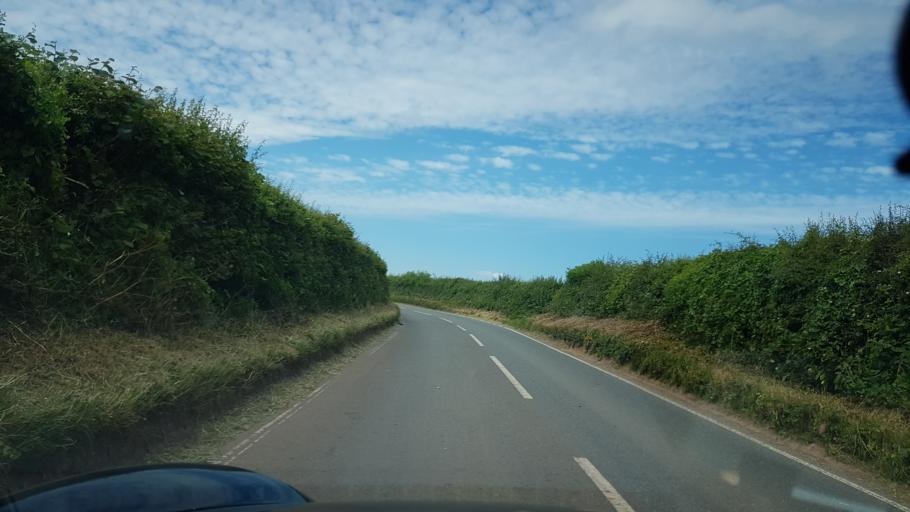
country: GB
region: Wales
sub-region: Carmarthenshire
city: Llanddowror
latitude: 51.7653
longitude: -4.5790
